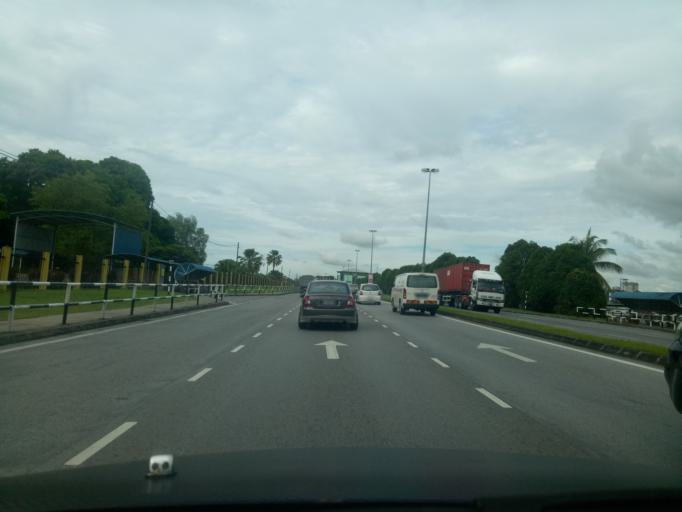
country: MY
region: Sarawak
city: Kuching
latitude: 1.5471
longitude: 110.3836
